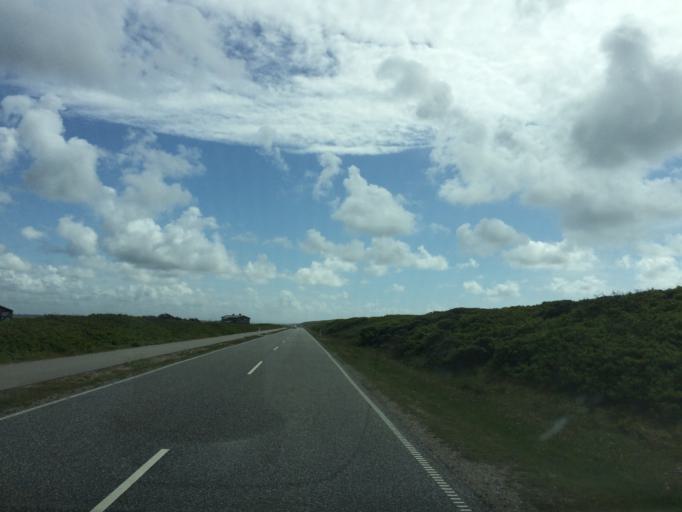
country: DK
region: Central Jutland
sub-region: Holstebro Kommune
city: Ulfborg
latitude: 56.3656
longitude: 8.1227
